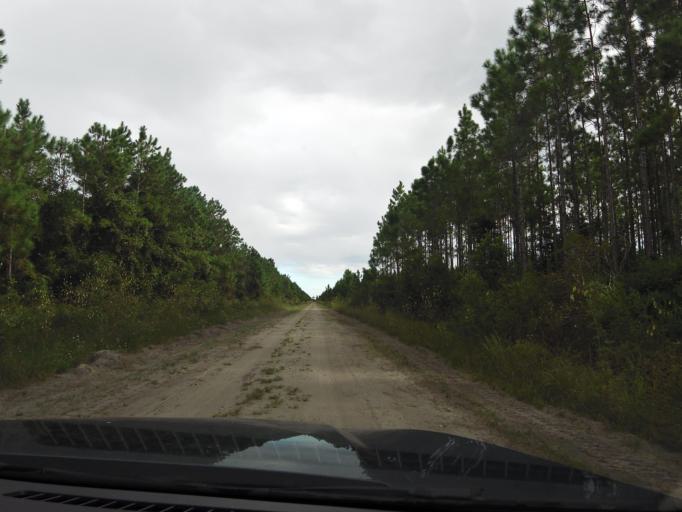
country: US
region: Florida
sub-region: Flagler County
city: Bunnell
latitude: 29.5532
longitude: -81.3291
